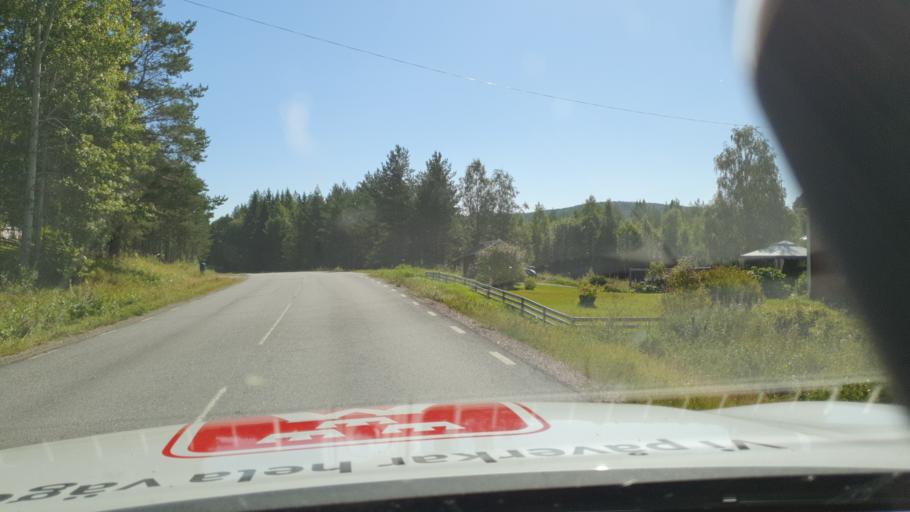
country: SE
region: Vaesterbotten
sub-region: Dorotea Kommun
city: Dorotea
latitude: 64.2655
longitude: 16.3552
